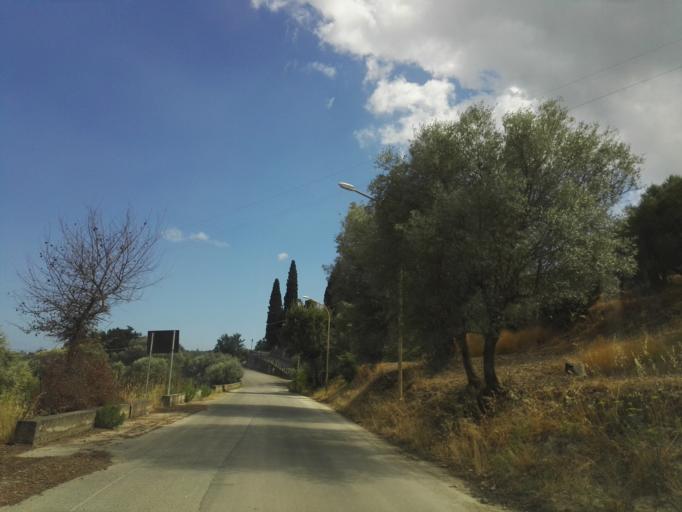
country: IT
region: Calabria
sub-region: Provincia di Reggio Calabria
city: Camini
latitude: 38.4294
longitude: 16.4860
